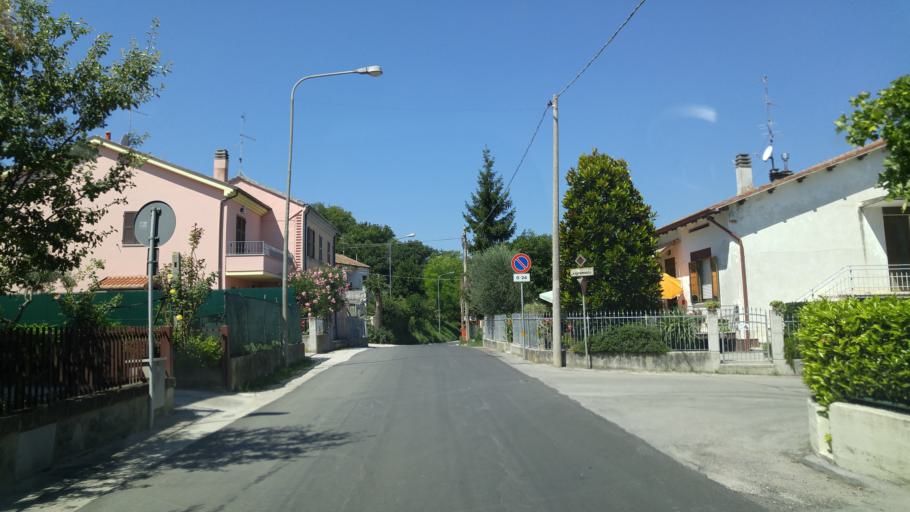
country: IT
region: The Marches
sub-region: Provincia di Pesaro e Urbino
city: Centinarola
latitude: 43.8323
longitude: 12.9818
